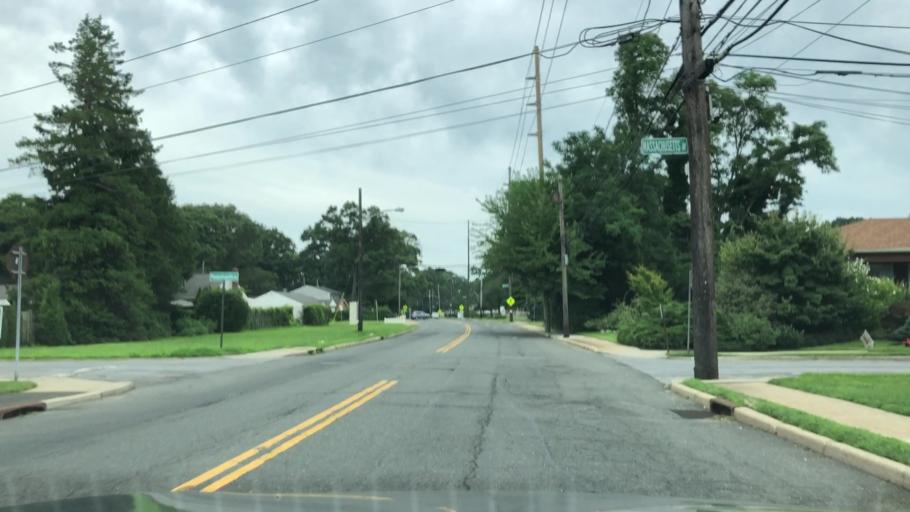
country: US
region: New York
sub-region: Nassau County
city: Massapequa
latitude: 40.6870
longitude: -73.4767
